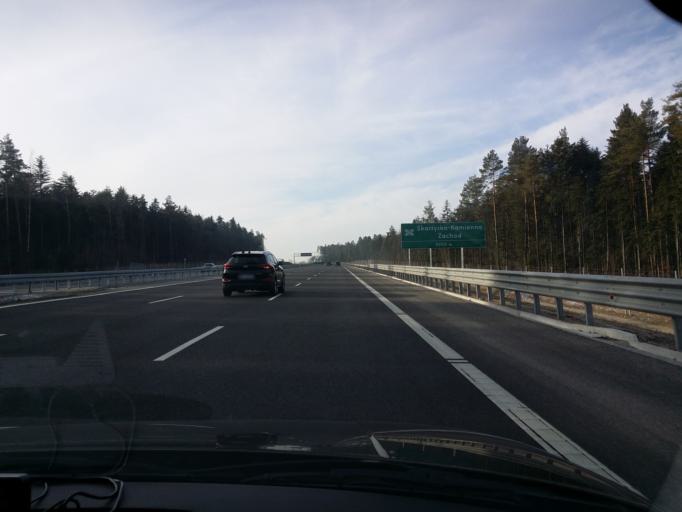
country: PL
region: Swietokrzyskie
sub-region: Powiat skarzyski
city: Skarzysko-Kamienna
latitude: 51.1507
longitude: 20.8423
